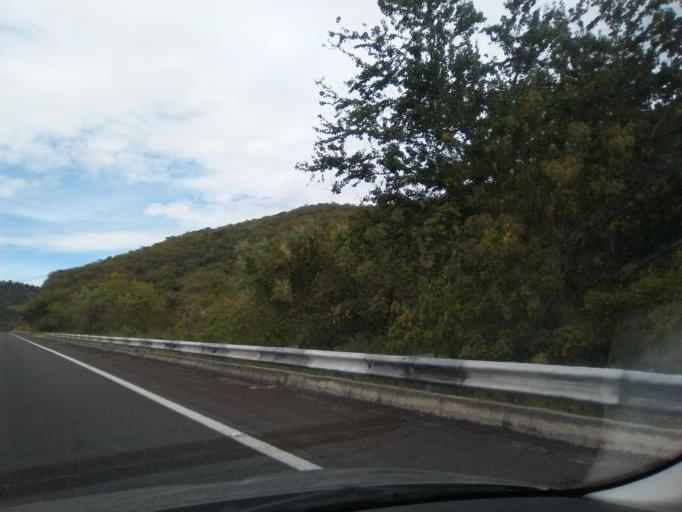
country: MX
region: Guerrero
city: Huitziltepec
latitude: 17.7259
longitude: -99.5010
